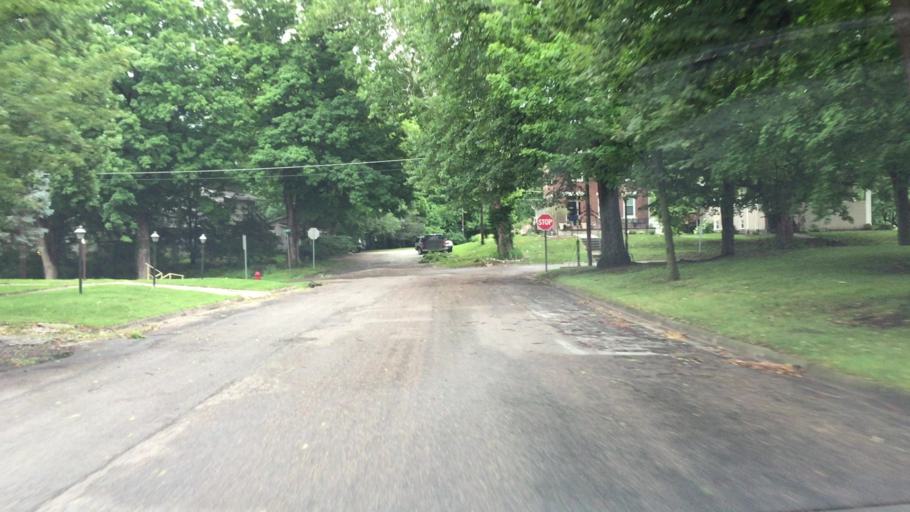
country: US
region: Illinois
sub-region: Hancock County
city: Warsaw
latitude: 40.3635
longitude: -91.4357
